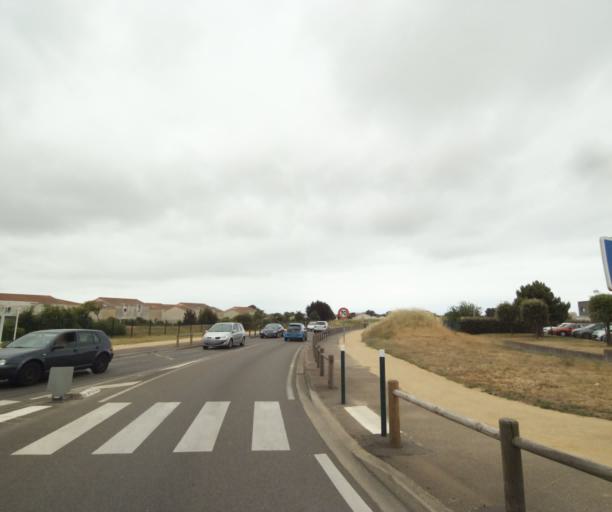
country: FR
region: Pays de la Loire
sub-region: Departement de la Vendee
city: Chateau-d'Olonne
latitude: 46.5071
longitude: -1.7570
